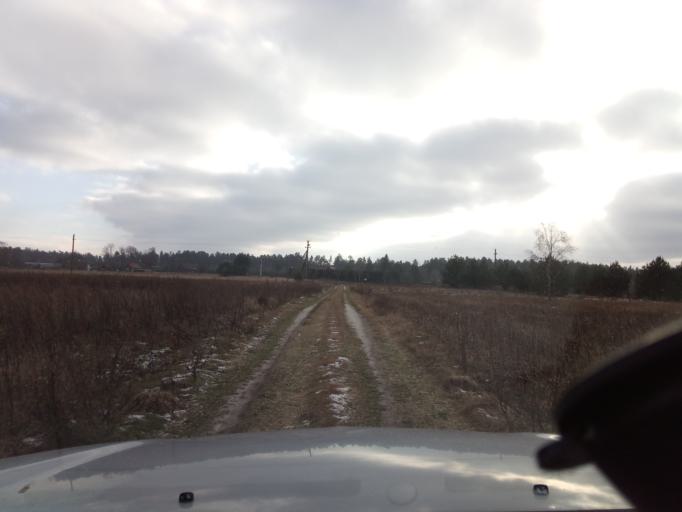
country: LT
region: Alytaus apskritis
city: Druskininkai
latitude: 54.1145
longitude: 24.2191
